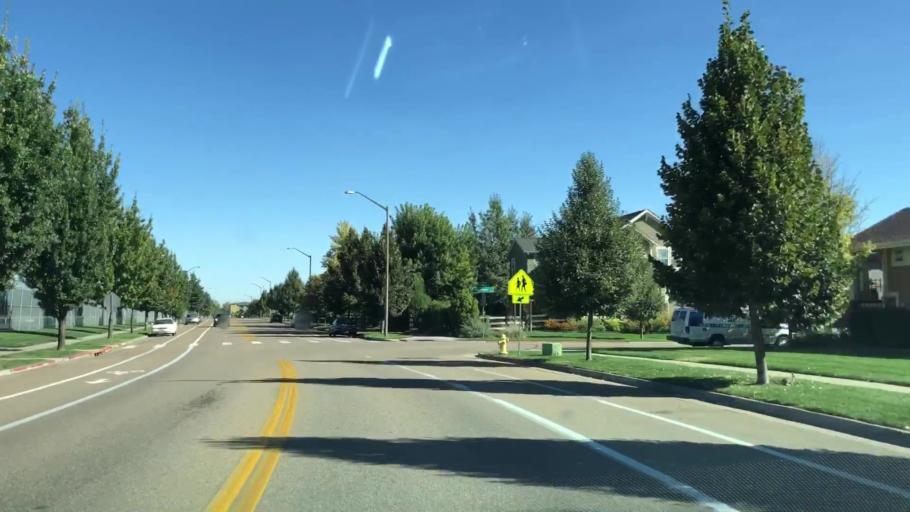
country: US
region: Colorado
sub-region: Larimer County
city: Fort Collins
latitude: 40.5120
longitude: -105.0104
